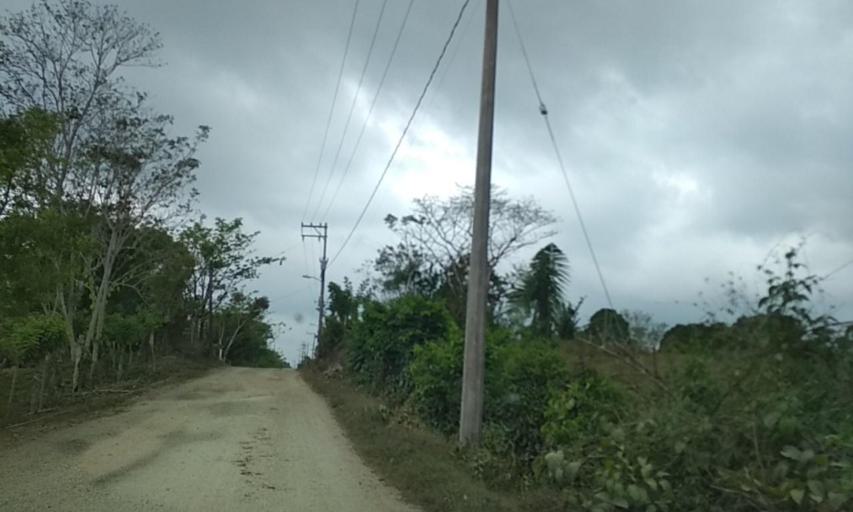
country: MX
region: Tabasco
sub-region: Huimanguillo
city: Francisco Rueda
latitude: 17.6541
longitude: -94.0934
